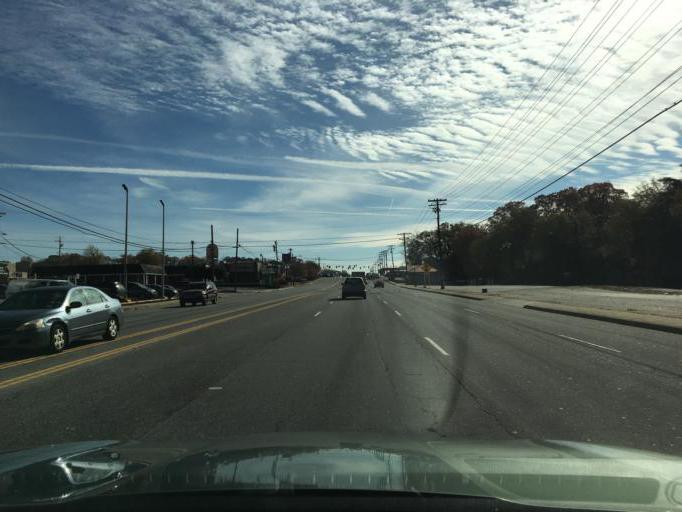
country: US
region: South Carolina
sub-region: Greenville County
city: Greenville
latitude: 34.8719
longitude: -82.3589
